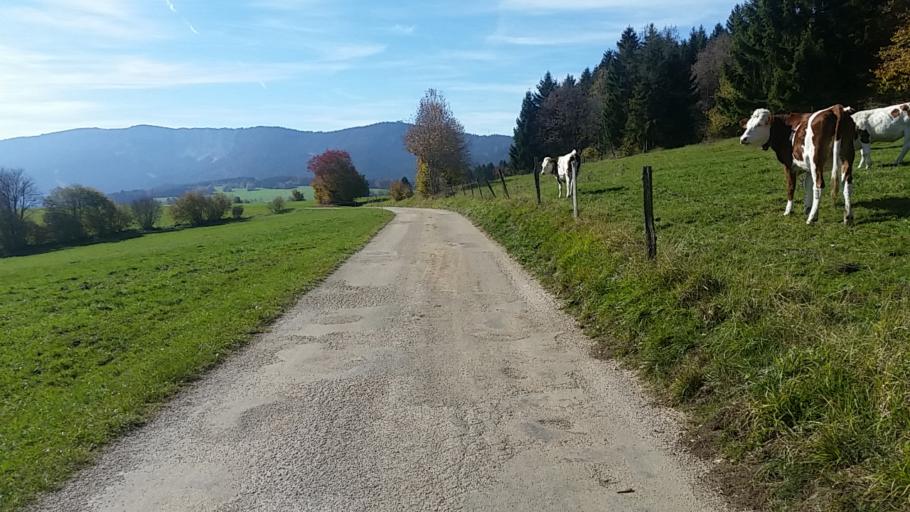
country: FR
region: Franche-Comte
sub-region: Departement du Doubs
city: Jougne
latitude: 46.7738
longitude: 6.4006
